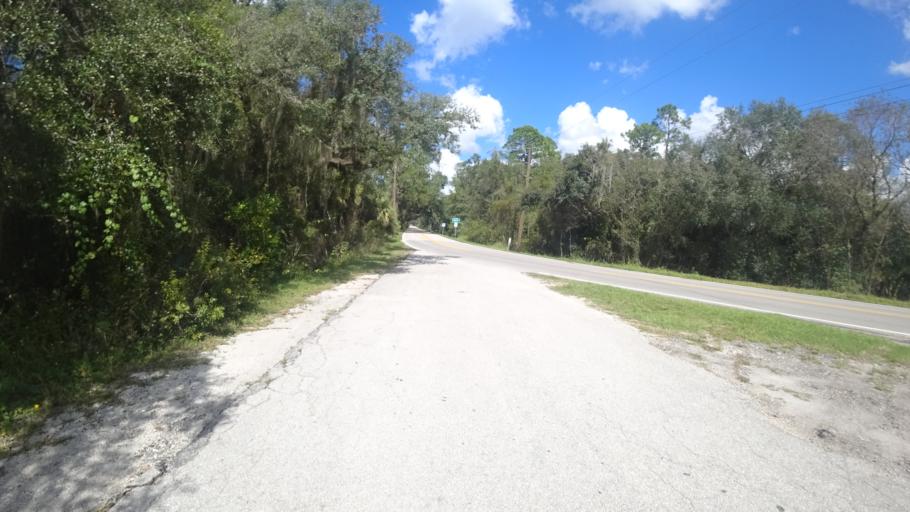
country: US
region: Florida
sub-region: Sarasota County
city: Lake Sarasota
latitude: 27.2907
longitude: -82.2531
